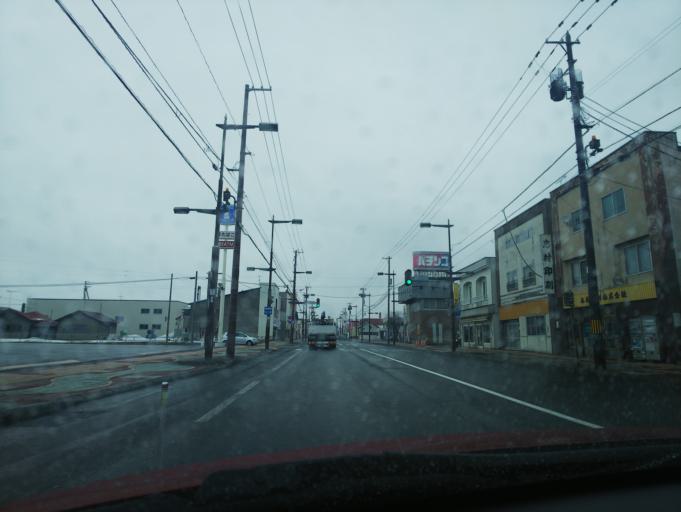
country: JP
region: Hokkaido
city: Nayoro
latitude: 44.1779
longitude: 142.3917
